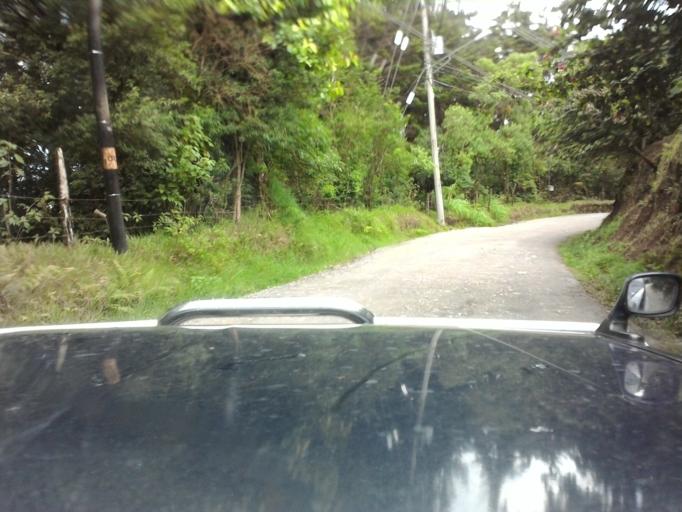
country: CR
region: Guanacaste
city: Juntas
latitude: 10.2997
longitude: -84.8043
